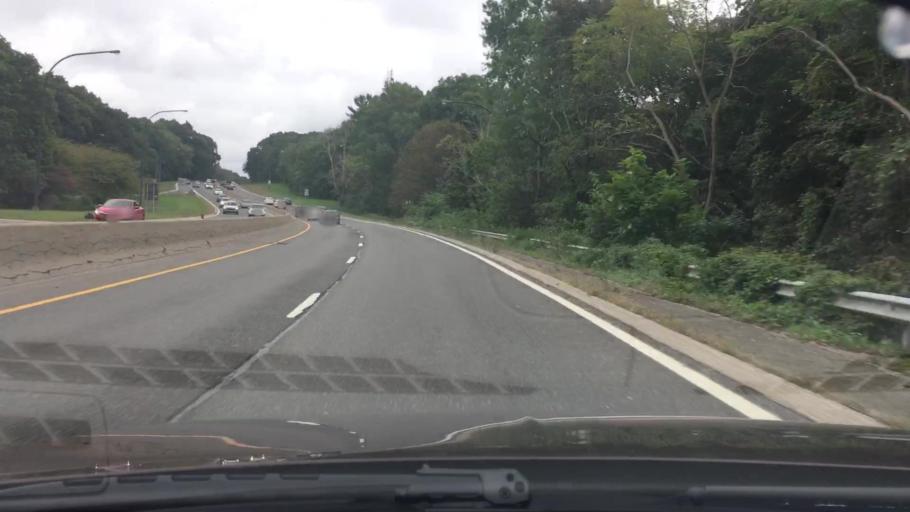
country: US
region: New York
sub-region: Suffolk County
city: West Hills
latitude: 40.8020
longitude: -73.4411
